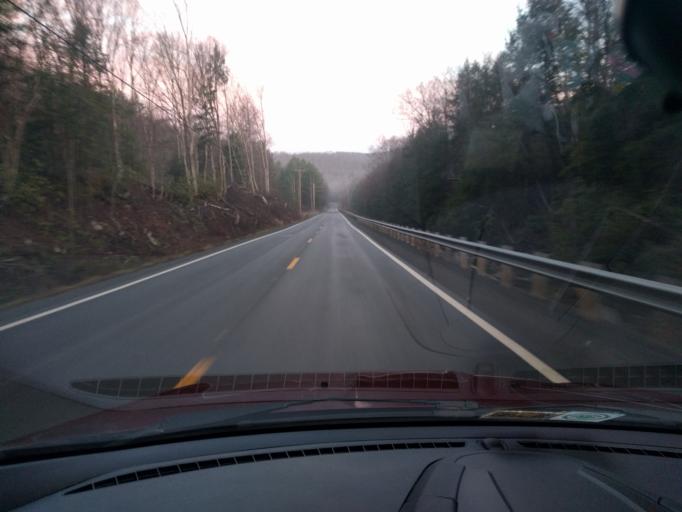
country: US
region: West Virginia
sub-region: Greenbrier County
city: Rainelle
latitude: 38.0448
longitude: -80.9244
